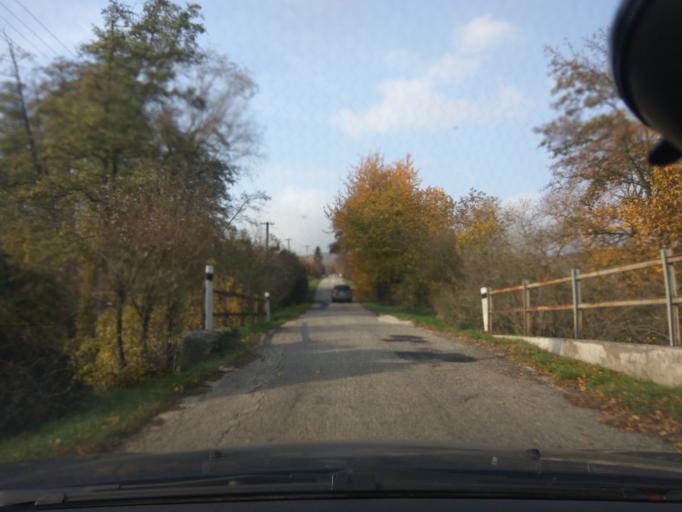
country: SK
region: Trnavsky
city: Vrbove
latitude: 48.6775
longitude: 17.7309
